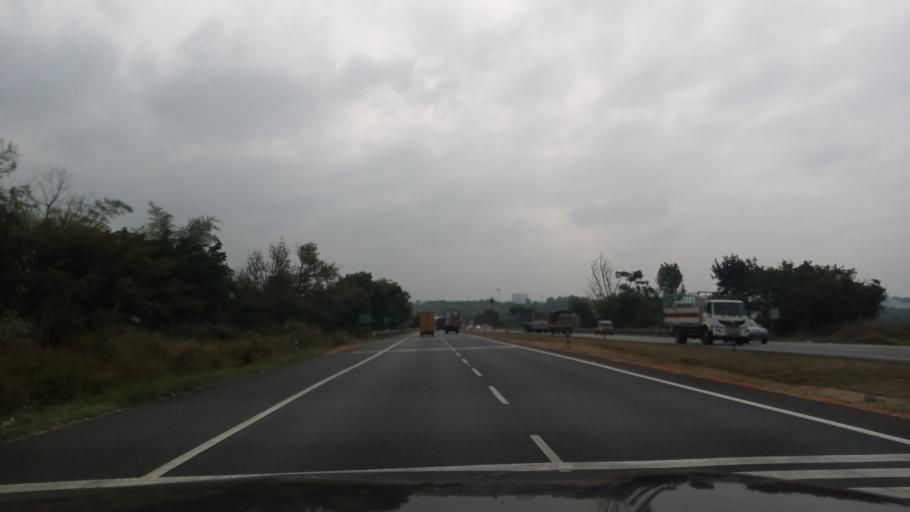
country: IN
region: Karnataka
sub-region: Bangalore Urban
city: Bangalore
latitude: 12.9096
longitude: 77.4680
